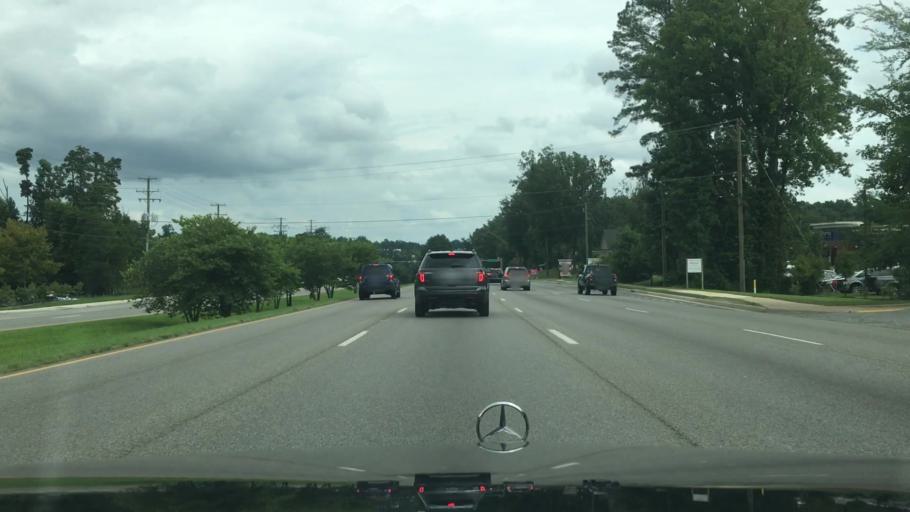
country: US
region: Virginia
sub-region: Chesterfield County
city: Brandermill
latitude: 37.4101
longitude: -77.6513
